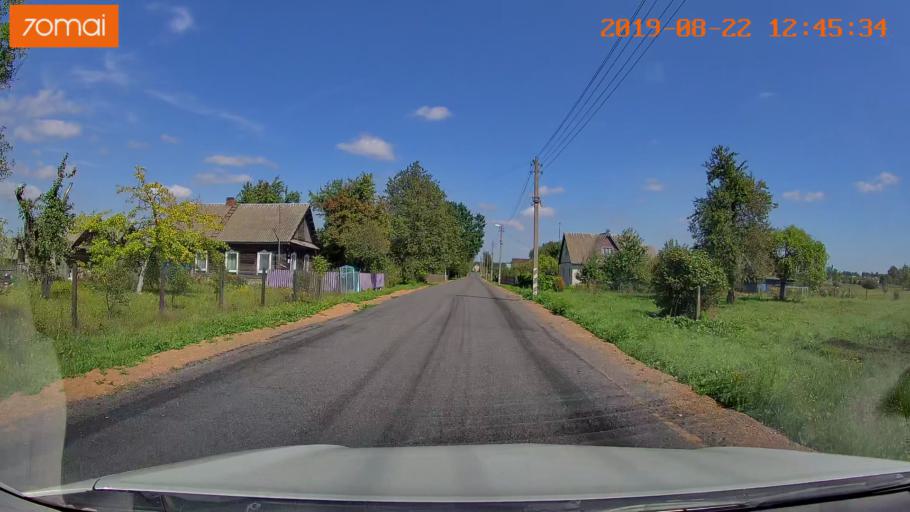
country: BY
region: Minsk
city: Prawdzinski
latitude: 53.4585
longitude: 27.6206
